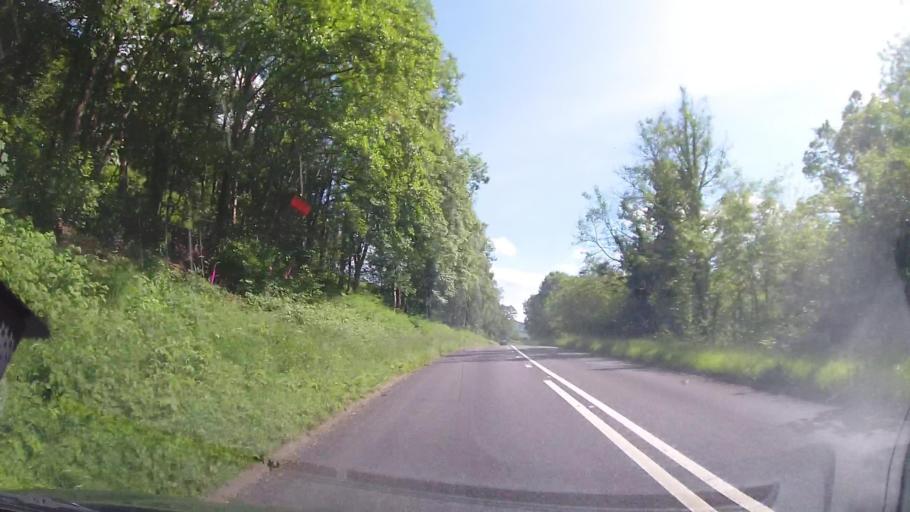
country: GB
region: Wales
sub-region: Gwynedd
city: Corris
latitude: 52.7076
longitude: -3.6864
